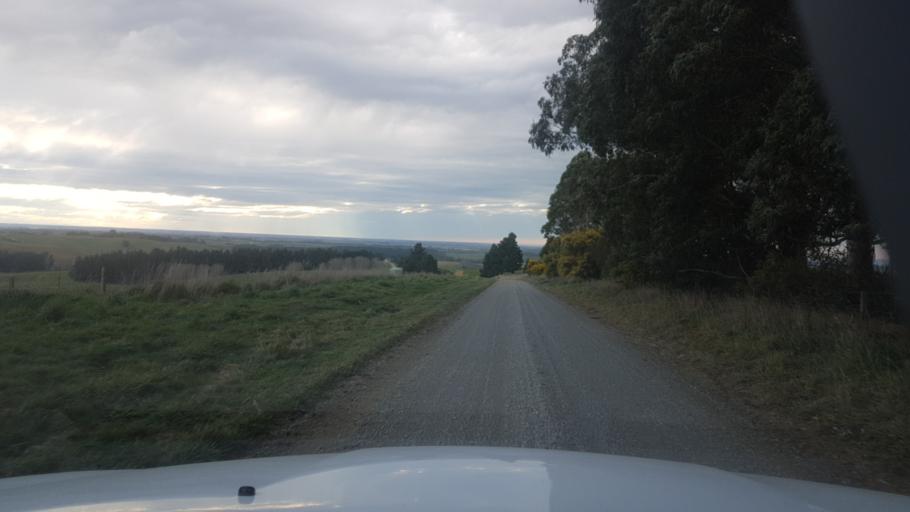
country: NZ
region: Canterbury
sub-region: Timaru District
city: Pleasant Point
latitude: -44.3450
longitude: 171.1360
